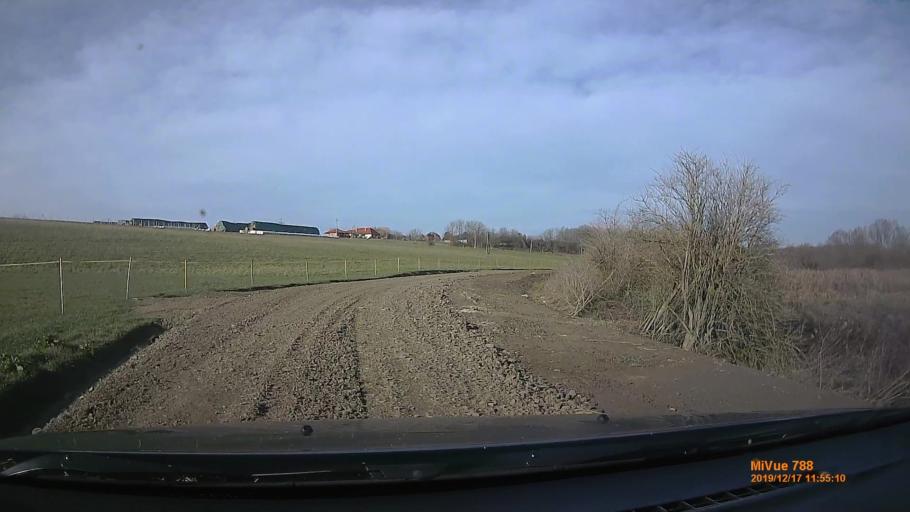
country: HU
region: Somogy
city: Kaposvar
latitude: 46.4526
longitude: 17.7697
